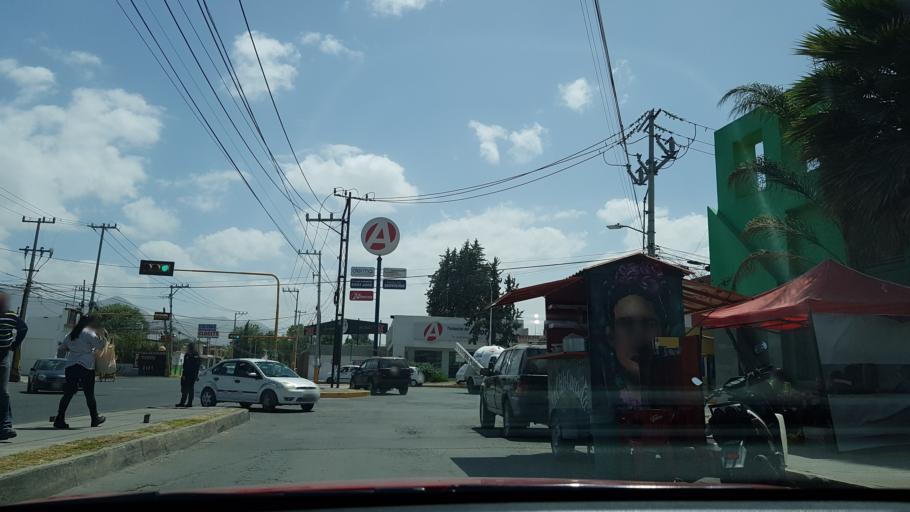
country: MX
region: Mexico
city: Santiago Teyahualco
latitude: 19.6631
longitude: -99.1299
